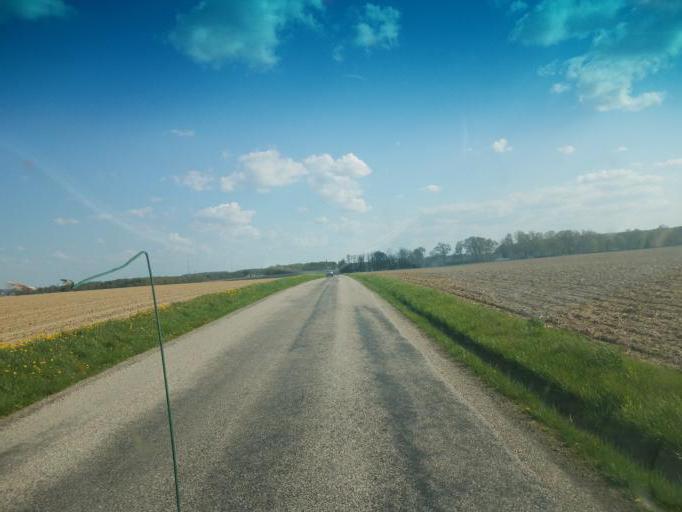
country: US
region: Ohio
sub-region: Wayne County
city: Smithville
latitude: 40.8487
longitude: -81.8779
